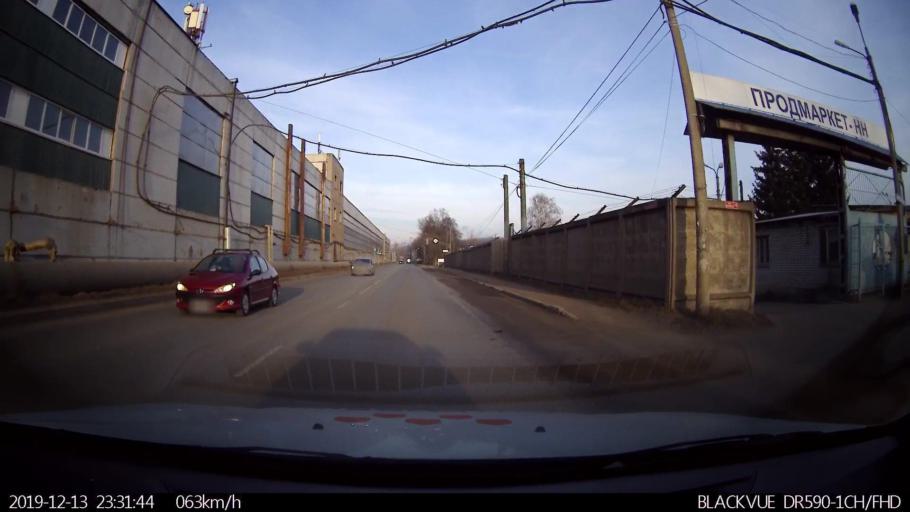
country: RU
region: Nizjnij Novgorod
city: Nizhniy Novgorod
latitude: 56.2688
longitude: 43.9453
